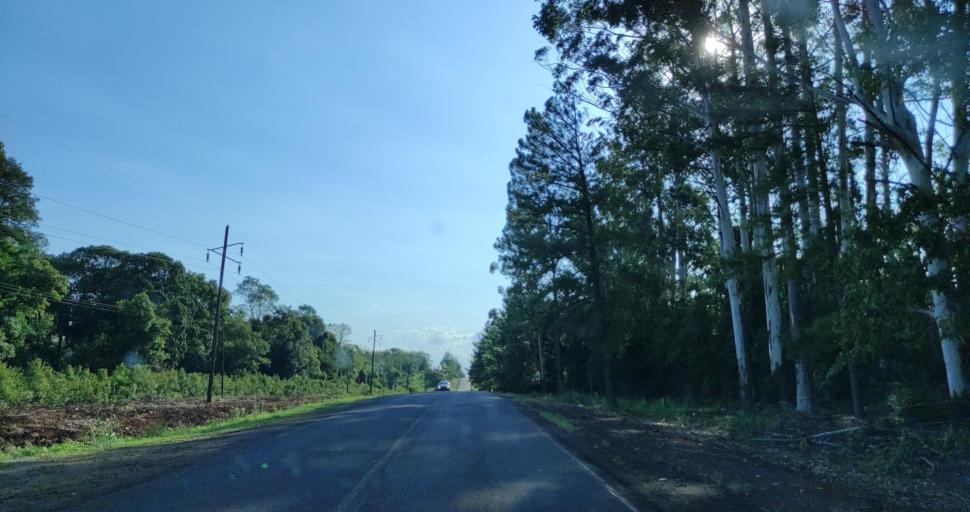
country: AR
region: Misiones
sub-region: Departamento de Eldorado
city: Eldorado
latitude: -26.4092
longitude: -54.4798
